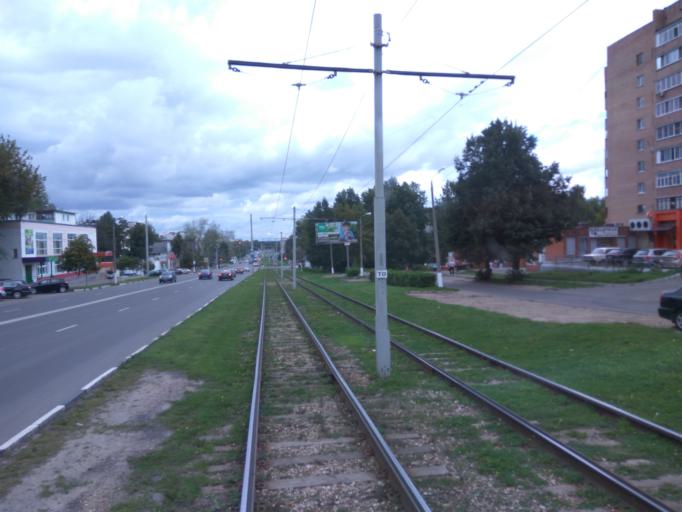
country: RU
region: Moskovskaya
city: Kolomna
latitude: 55.0859
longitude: 38.7647
